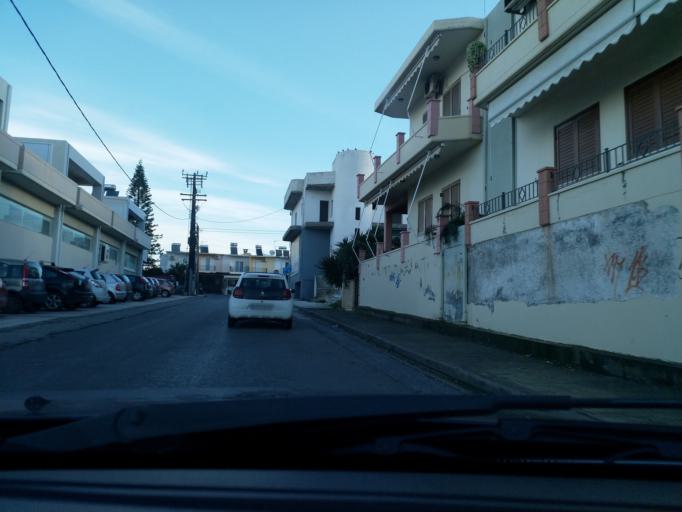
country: GR
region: Crete
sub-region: Nomos Chanias
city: Chania
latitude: 35.5130
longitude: 24.0475
